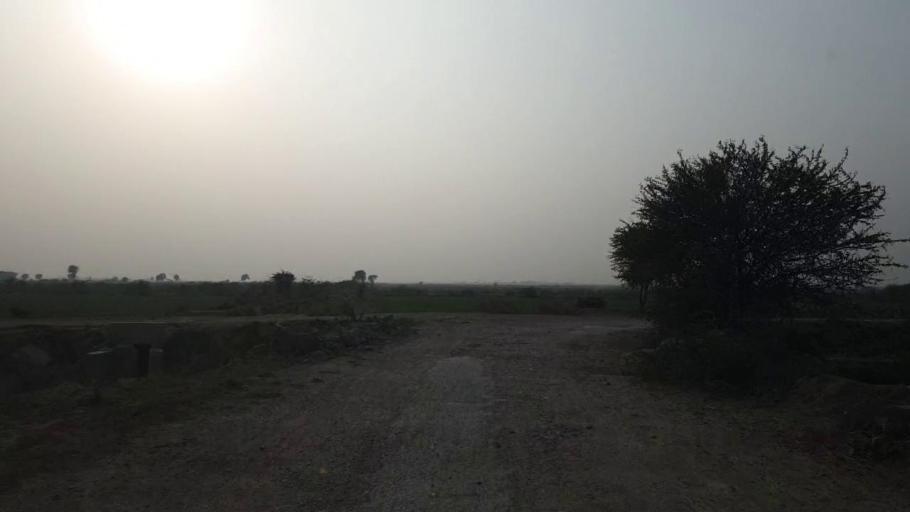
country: PK
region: Sindh
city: Mirpur Batoro
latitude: 24.6544
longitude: 68.3788
